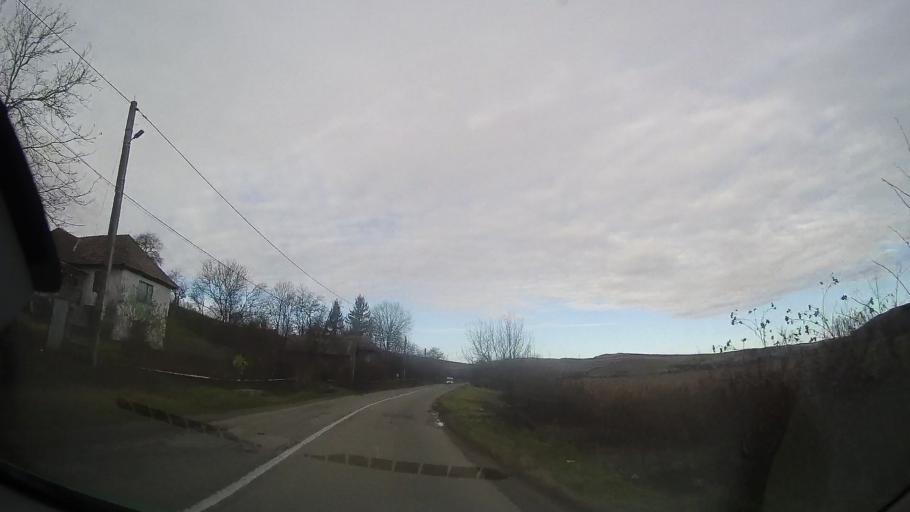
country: RO
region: Cluj
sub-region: Comuna Geaca
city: Geaca
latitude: 46.8330
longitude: 24.1322
